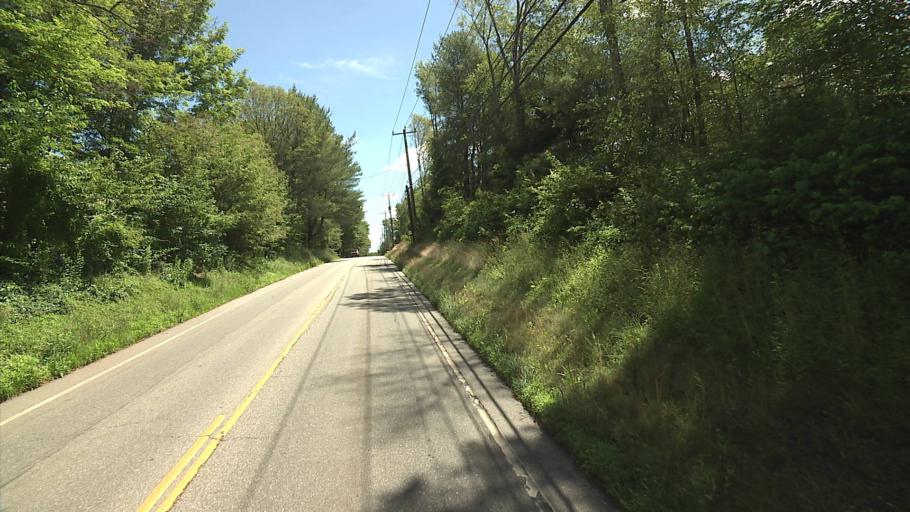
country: US
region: Rhode Island
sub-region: Washington County
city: Ashaway
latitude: 41.4361
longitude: -71.8178
